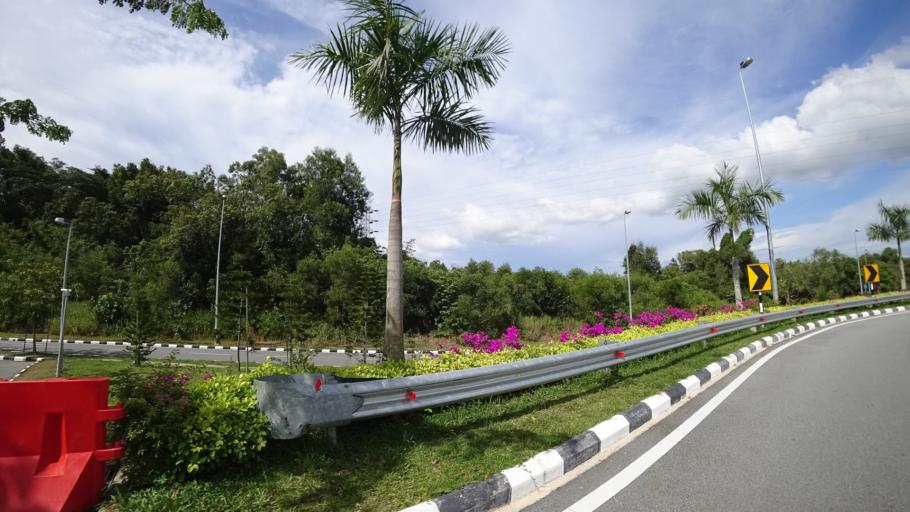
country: BN
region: Brunei and Muara
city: Bandar Seri Begawan
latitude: 4.9451
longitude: 114.9362
